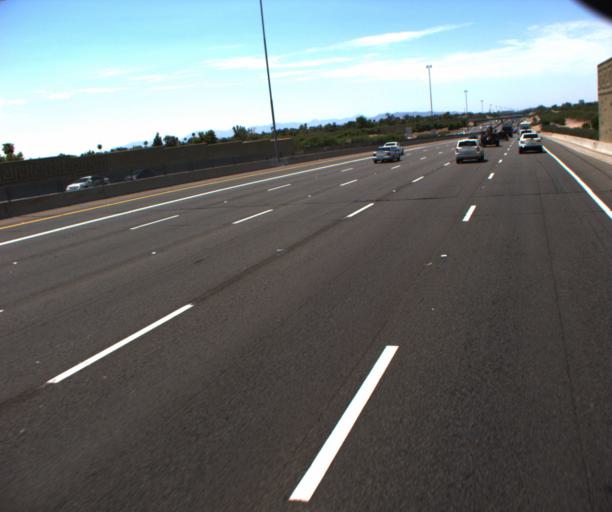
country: US
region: Arizona
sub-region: Maricopa County
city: Gilbert
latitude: 33.3866
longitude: -111.7713
